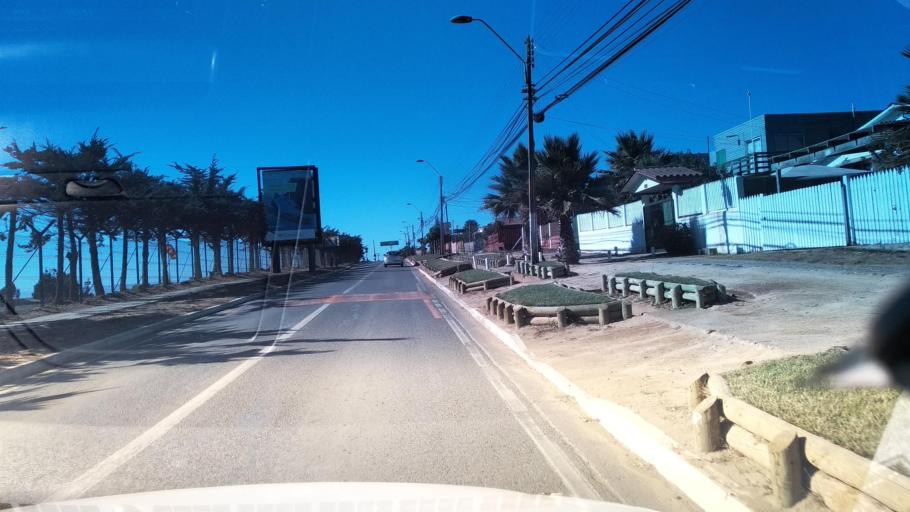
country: CL
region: O'Higgins
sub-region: Provincia de Colchagua
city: Santa Cruz
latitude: -34.3952
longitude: -72.0181
